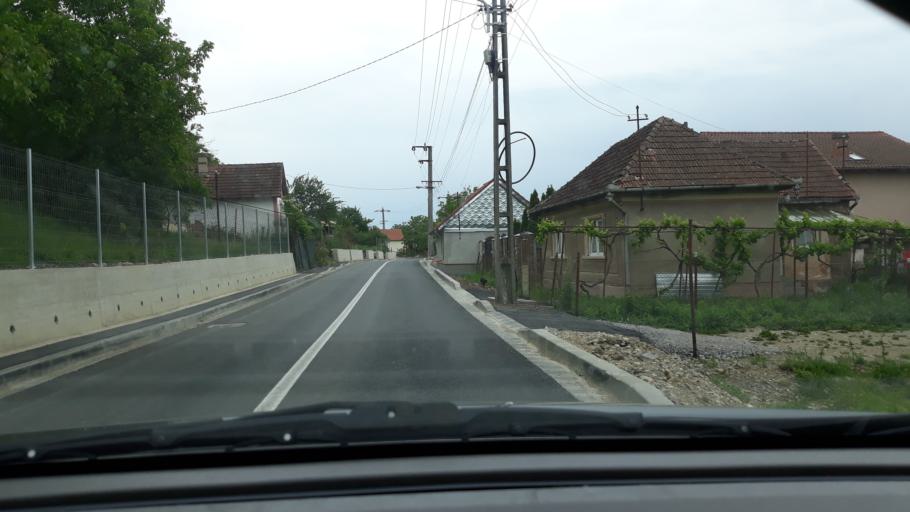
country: RO
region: Bihor
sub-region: Comuna Osorheiu
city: Osorheiu
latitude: 47.0589
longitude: 22.0093
